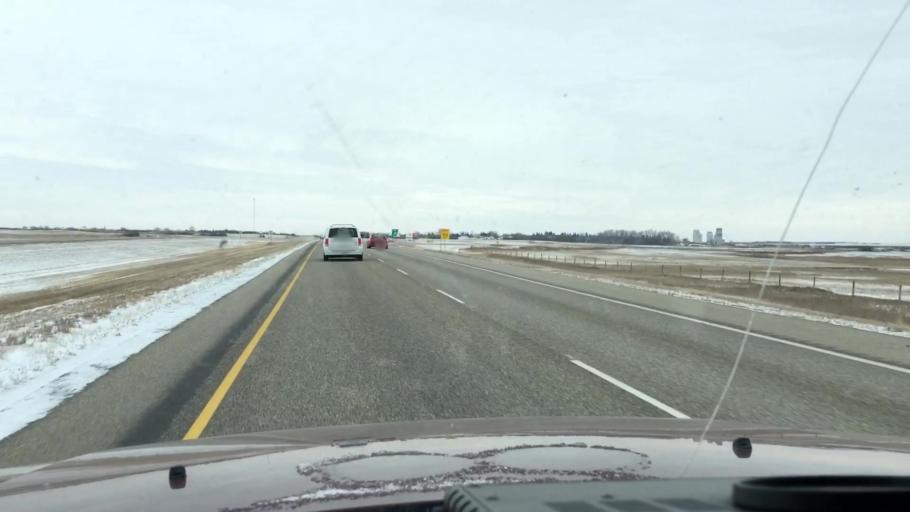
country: CA
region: Saskatchewan
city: Saskatoon
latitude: 51.5167
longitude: -106.2874
